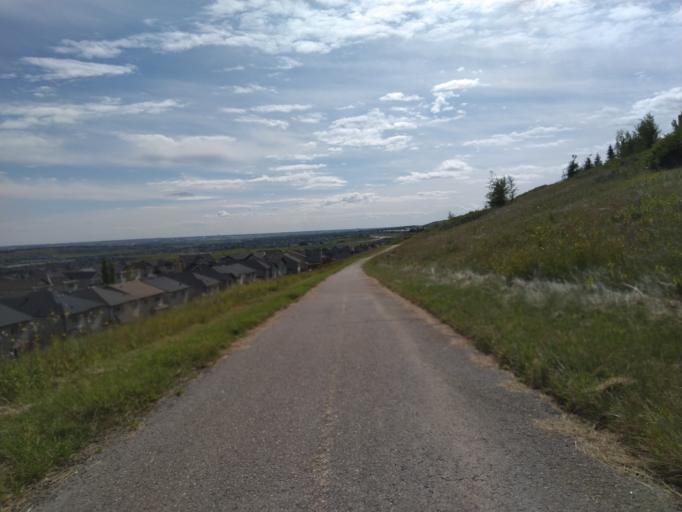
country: CA
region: Alberta
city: Calgary
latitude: 51.1579
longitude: -114.1561
